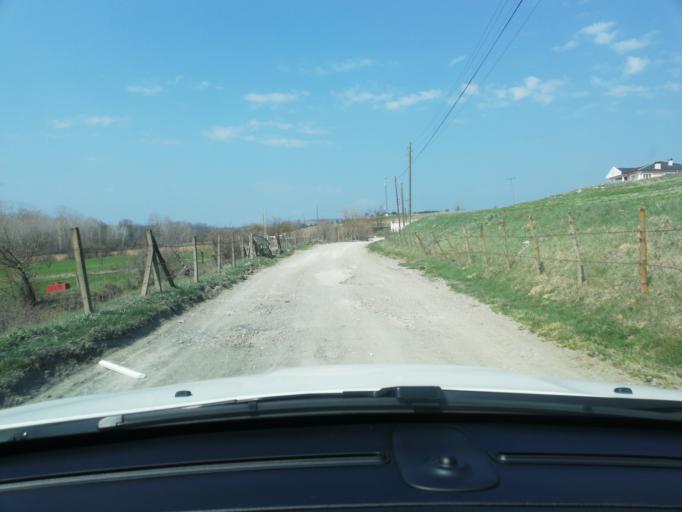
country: TR
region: Kastamonu
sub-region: Cide
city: Kastamonu
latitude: 41.4603
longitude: 33.7552
